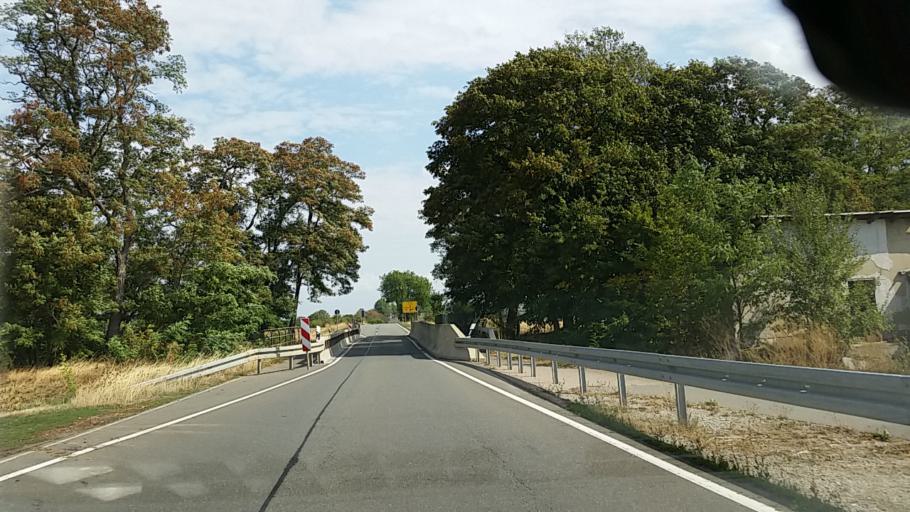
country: DE
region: Saxony-Anhalt
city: Querfurt
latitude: 51.3554
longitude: 11.5416
